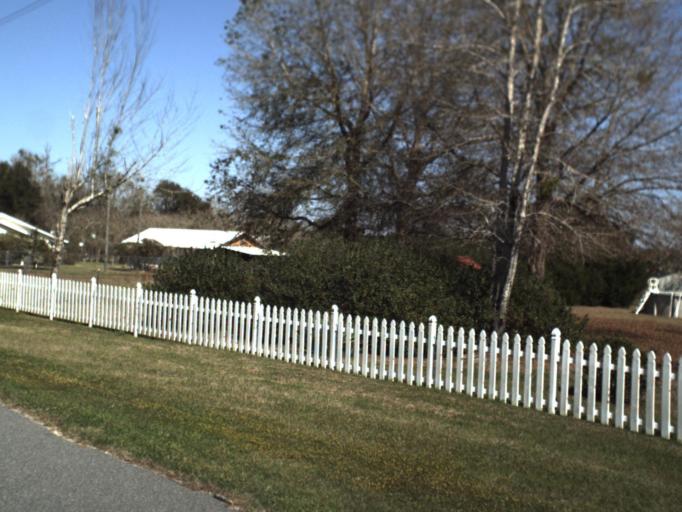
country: US
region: Florida
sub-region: Calhoun County
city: Blountstown
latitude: 30.3025
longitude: -85.1290
